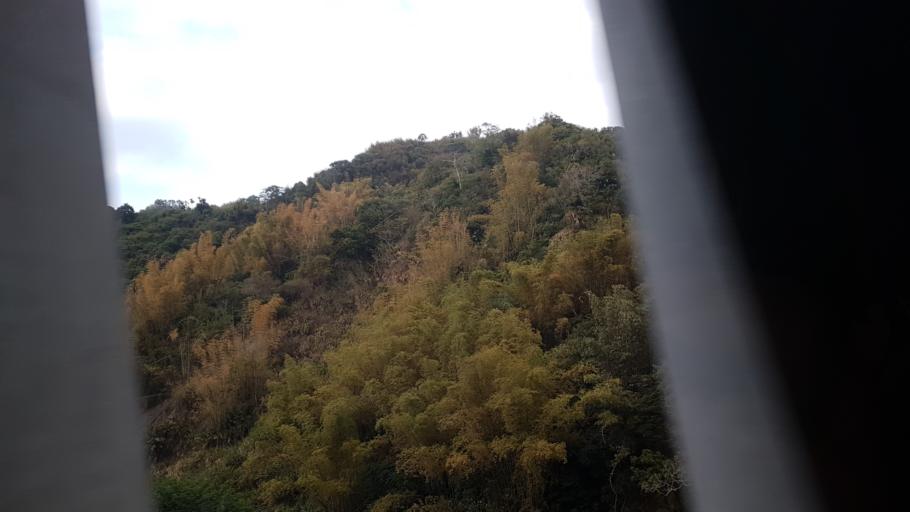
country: TW
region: Taiwan
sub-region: Chiayi
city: Jiayi Shi
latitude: 23.3406
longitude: 120.4966
